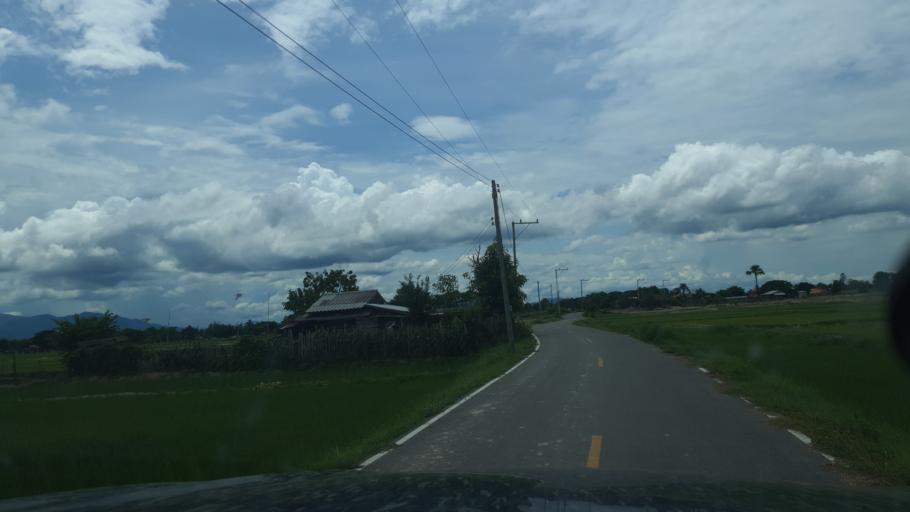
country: TH
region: Lampang
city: Sop Prap
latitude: 17.8733
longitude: 99.3855
